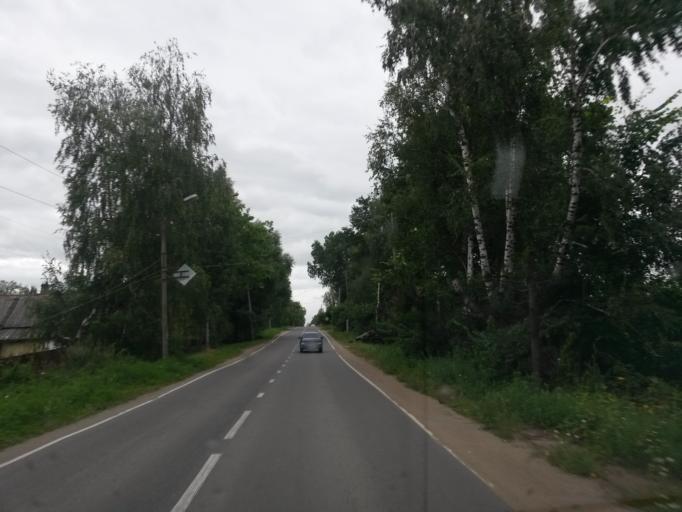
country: RU
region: Jaroslavl
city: Tutayev
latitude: 57.8874
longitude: 39.5397
